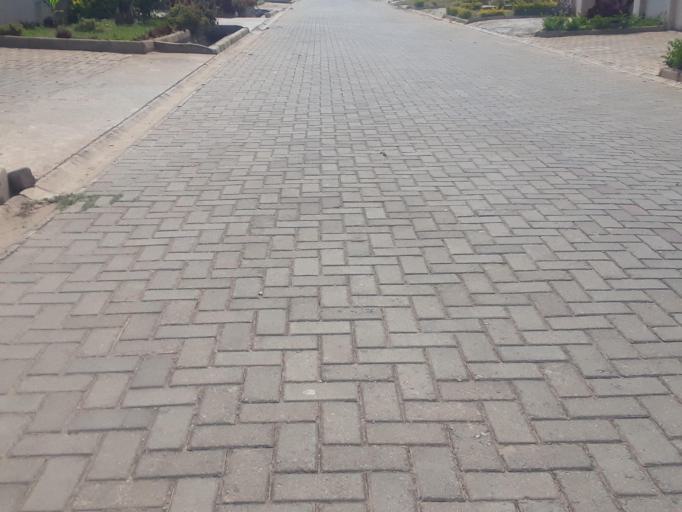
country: ZM
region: Lusaka
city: Lusaka
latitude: -15.3597
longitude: 28.2816
